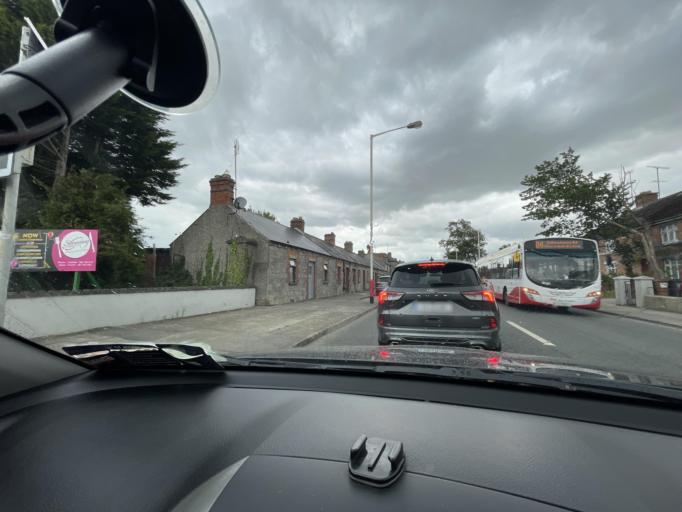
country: IE
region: Leinster
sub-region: Lu
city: Drogheda
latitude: 53.7221
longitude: -6.3604
